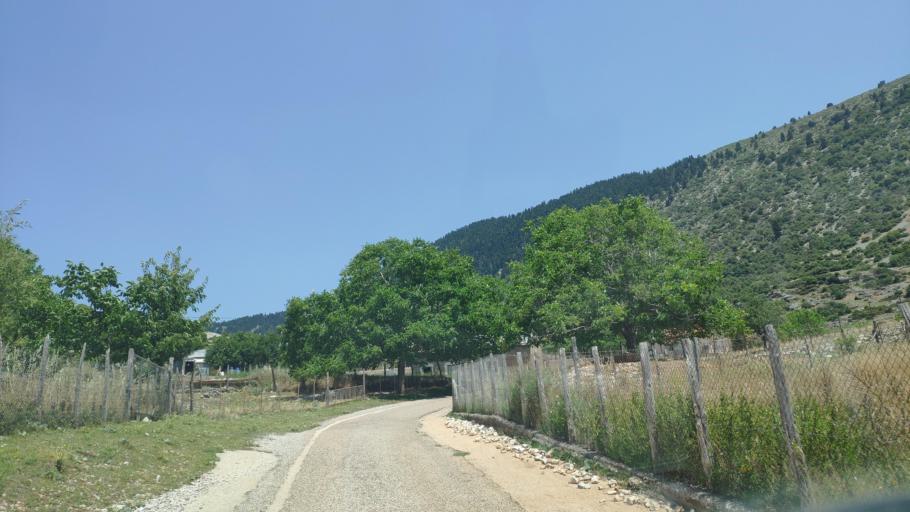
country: GR
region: West Greece
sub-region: Nomos Aitolias kai Akarnanias
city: Krikellos
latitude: 39.0527
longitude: 21.3671
